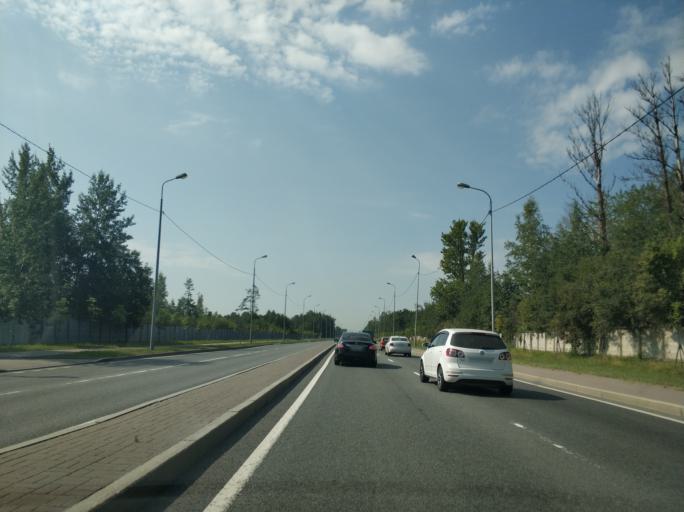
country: RU
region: St.-Petersburg
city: Krasnogvargeisky
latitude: 59.9913
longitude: 30.5318
